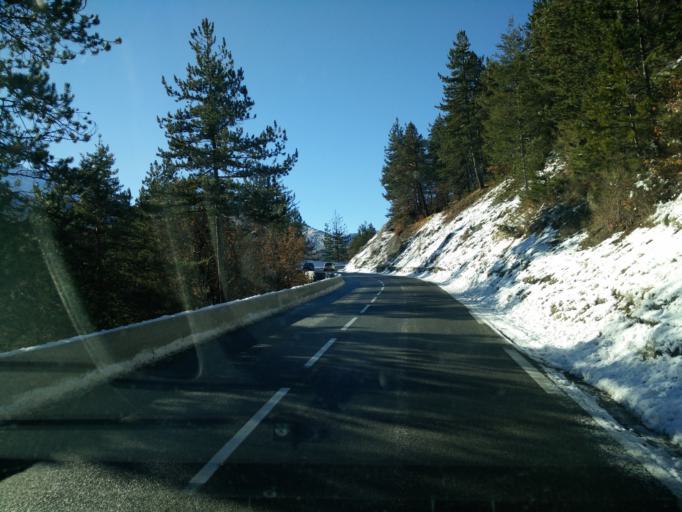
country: FR
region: Provence-Alpes-Cote d'Azur
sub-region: Departement des Alpes-de-Haute-Provence
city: Annot
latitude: 43.9346
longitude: 6.6351
